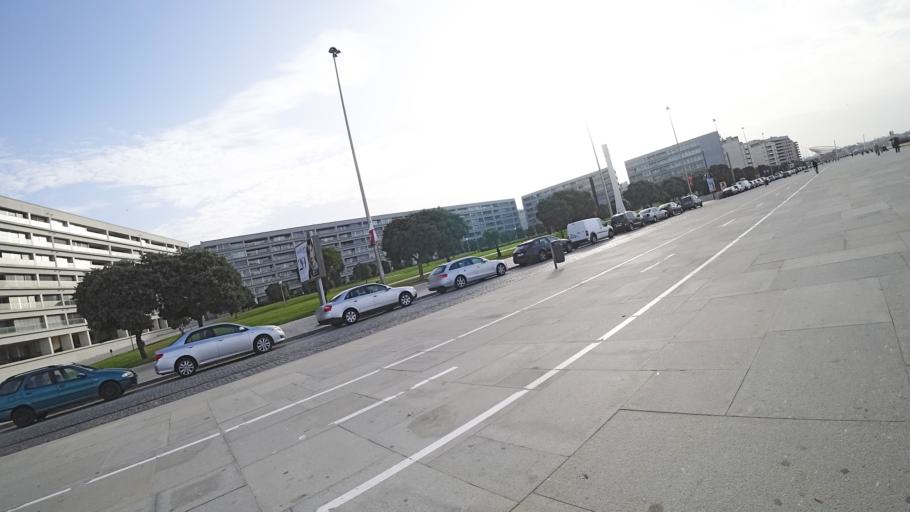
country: PT
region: Porto
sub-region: Matosinhos
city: Matosinhos
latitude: 41.1791
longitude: -8.6934
